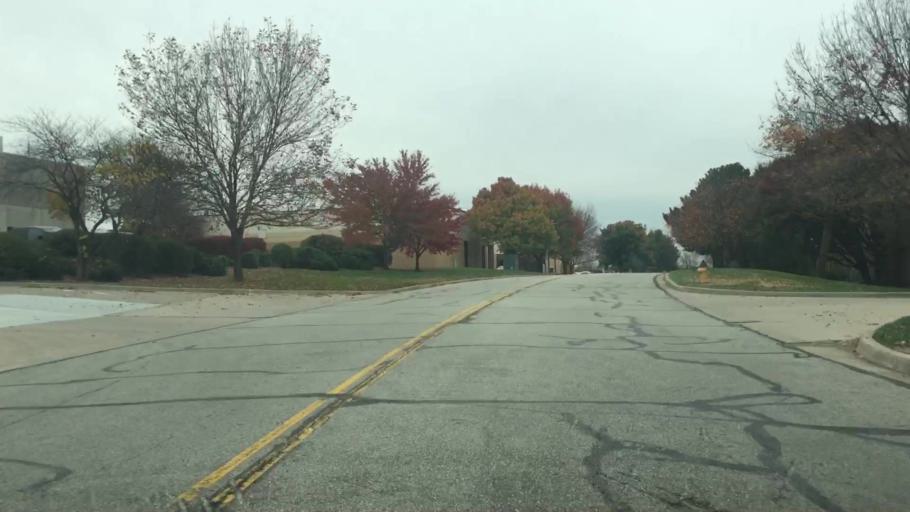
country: US
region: Kansas
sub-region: Johnson County
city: Lenexa
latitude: 38.9304
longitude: -94.7759
